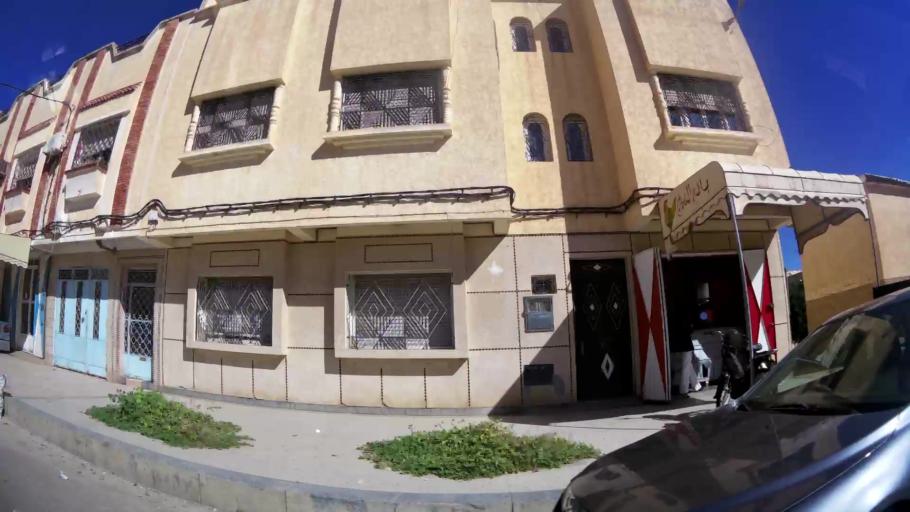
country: MA
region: Oriental
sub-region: Oujda-Angad
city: Oujda
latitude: 34.6574
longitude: -1.8952
